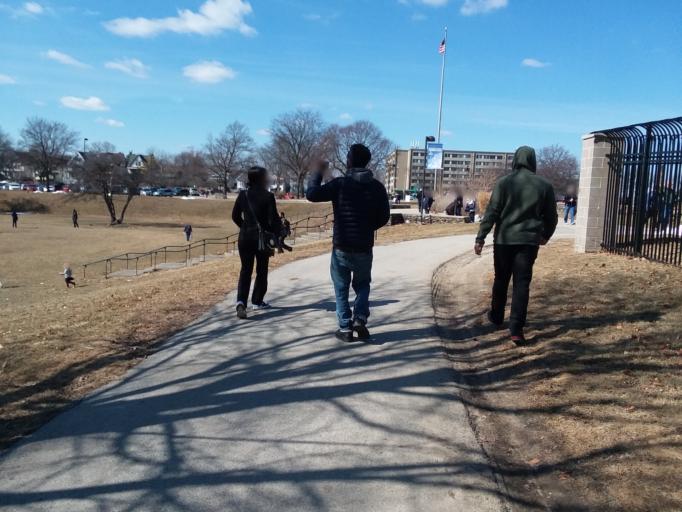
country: US
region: Wisconsin
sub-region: Milwaukee County
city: West Milwaukee
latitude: 43.0257
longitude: -87.9451
